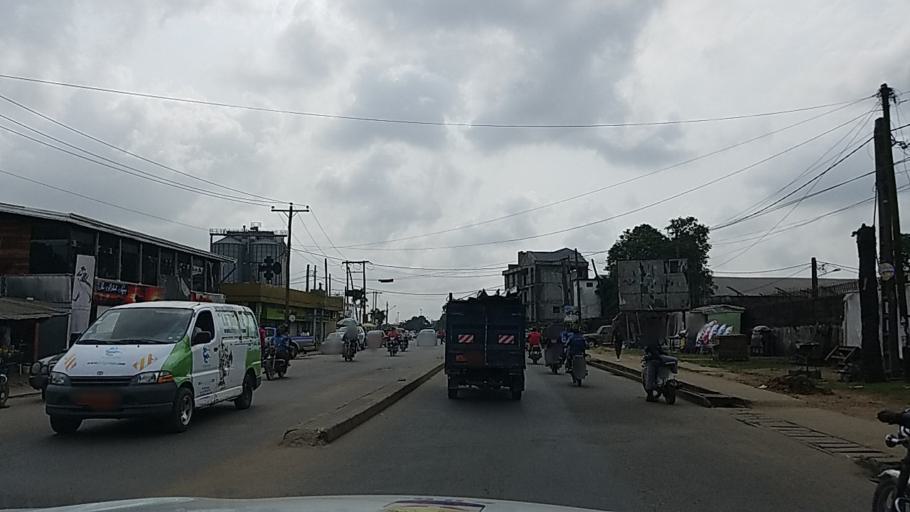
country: CM
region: Littoral
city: Douala
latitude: 4.0488
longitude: 9.7404
